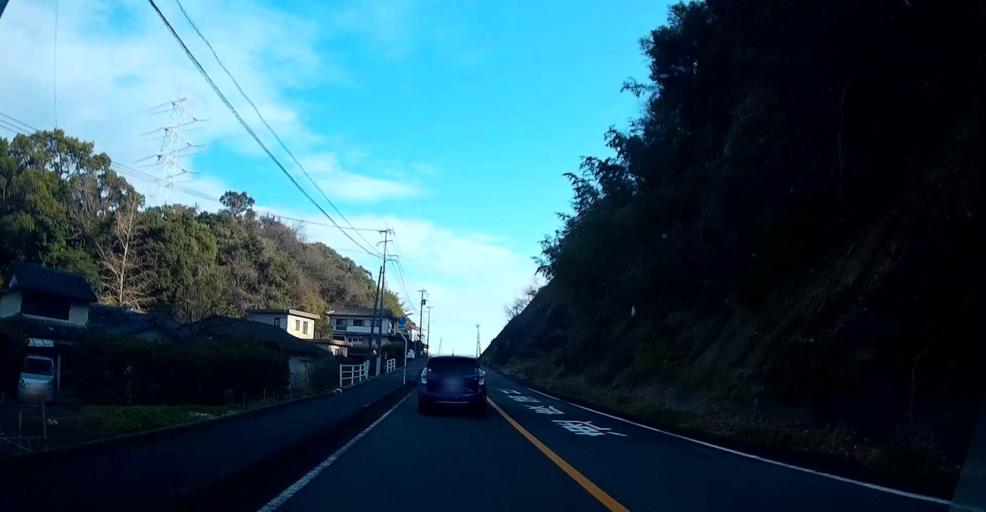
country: JP
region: Kumamoto
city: Yatsushiro
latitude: 32.5177
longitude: 130.4537
